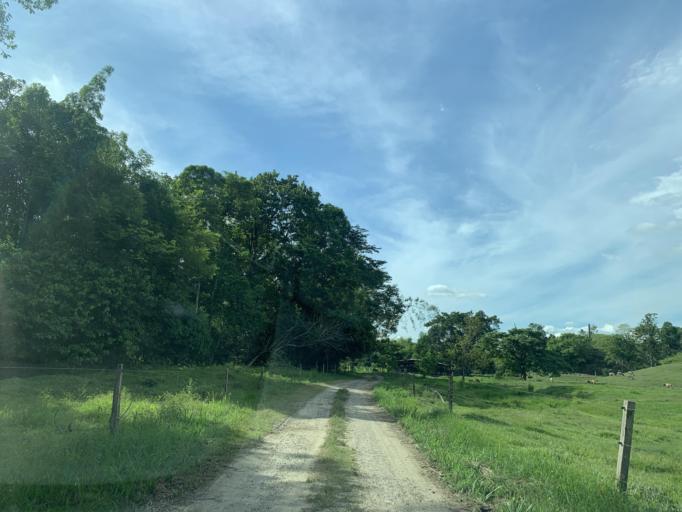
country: CO
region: Boyaca
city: Puerto Boyaca
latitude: 6.0129
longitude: -74.3945
